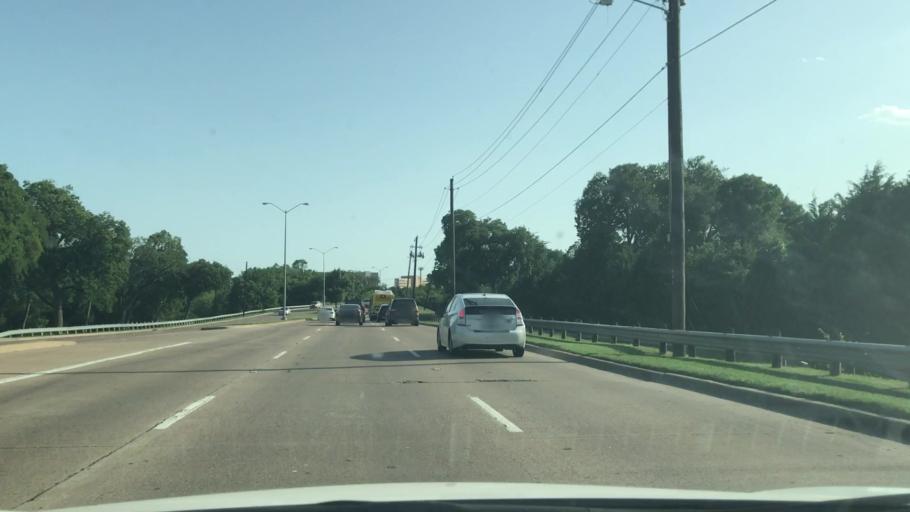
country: US
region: Texas
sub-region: Dallas County
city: Richardson
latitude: 32.8927
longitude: -96.7539
